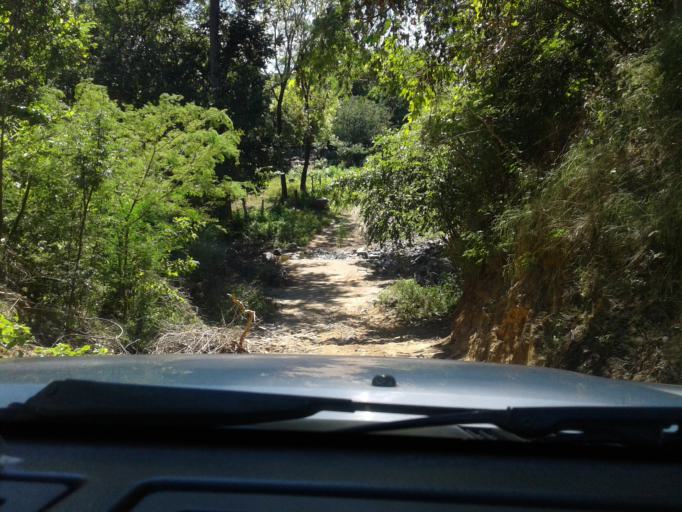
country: NI
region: Carazo
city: Santa Teresa
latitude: 11.6246
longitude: -86.1993
